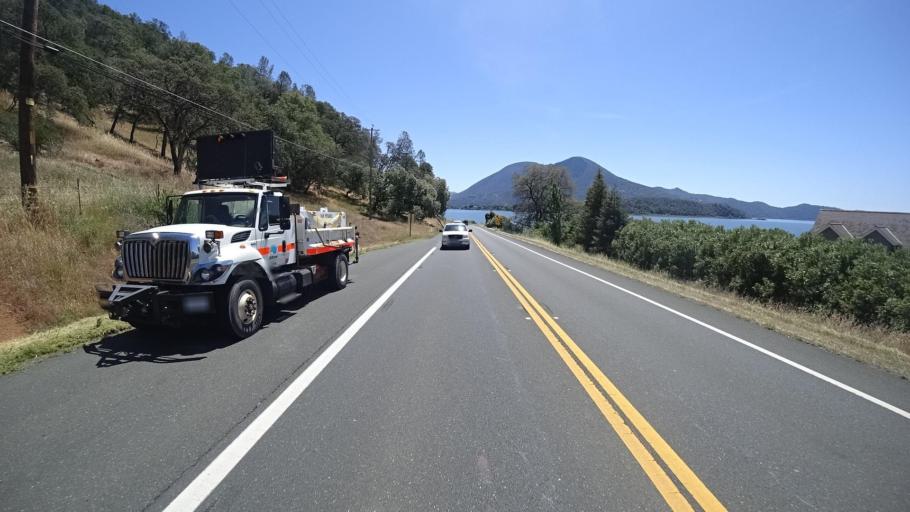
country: US
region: California
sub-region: Lake County
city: Soda Bay
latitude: 39.0372
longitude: -122.7453
